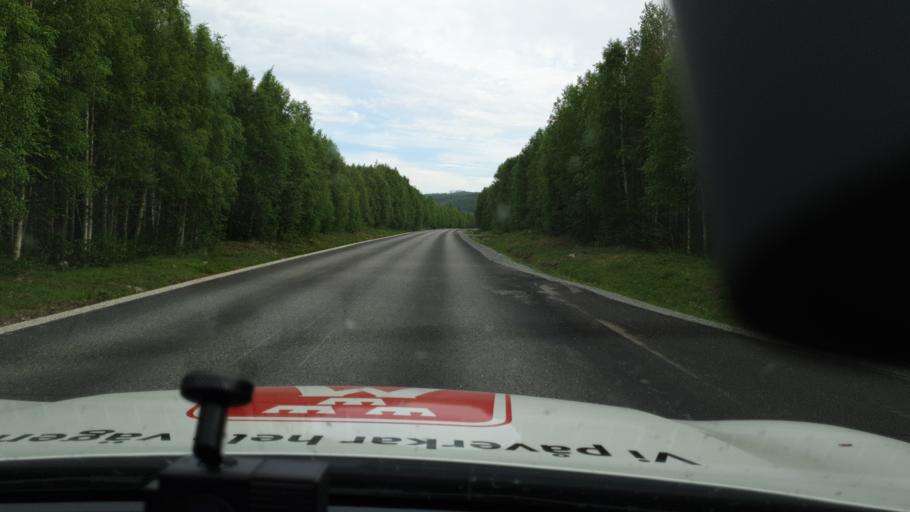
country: SE
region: Vaesterbotten
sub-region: Mala Kommun
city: Mala
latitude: 64.9293
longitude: 18.6185
